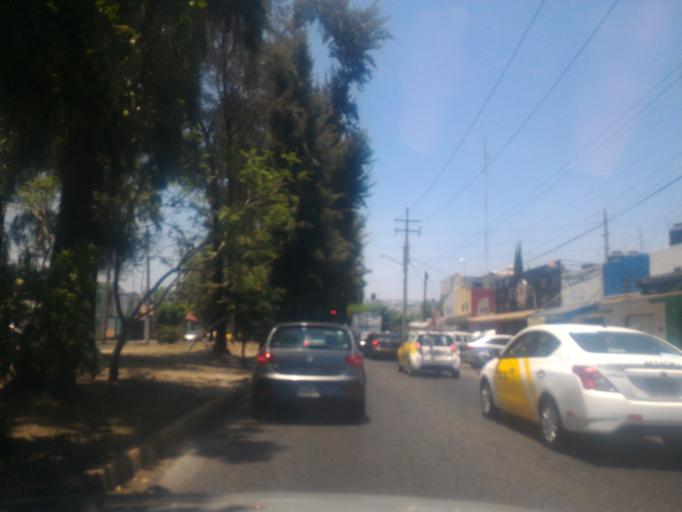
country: MX
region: Jalisco
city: Tlaquepaque
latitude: 20.6649
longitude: -103.2980
